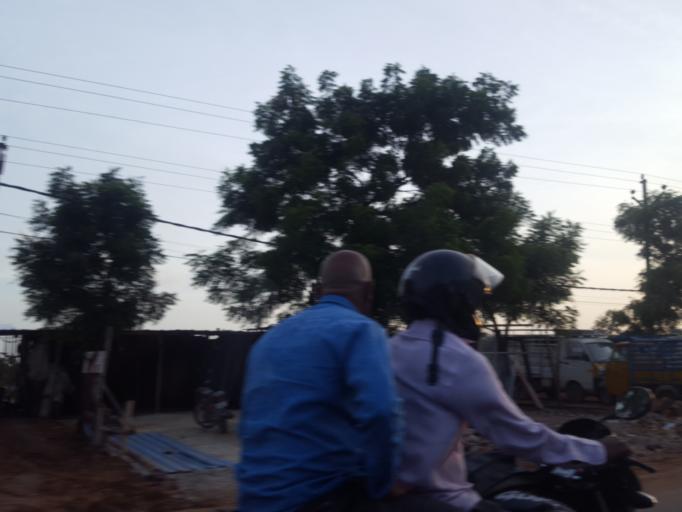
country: IN
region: Telangana
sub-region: Rangareddi
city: Kukatpalli
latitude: 17.5412
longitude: 78.3904
